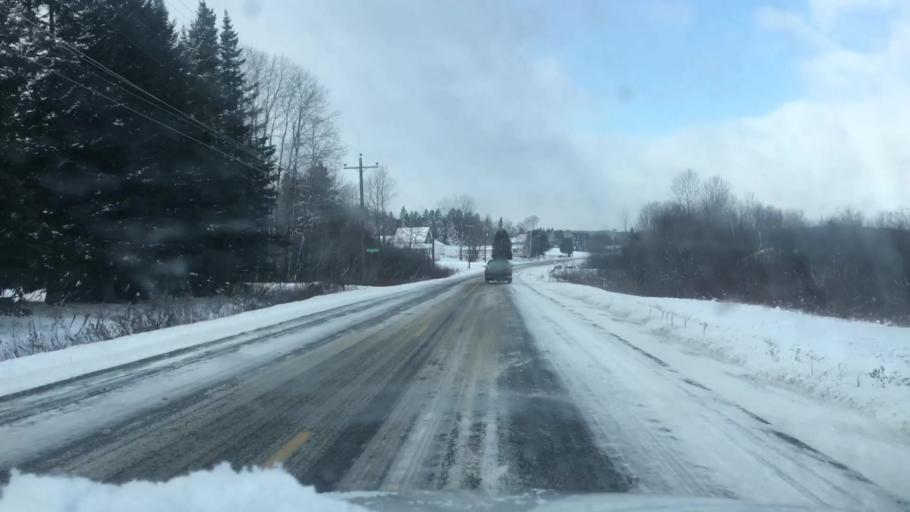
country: CA
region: New Brunswick
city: Harrison Brook
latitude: 47.2064
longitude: -67.9918
